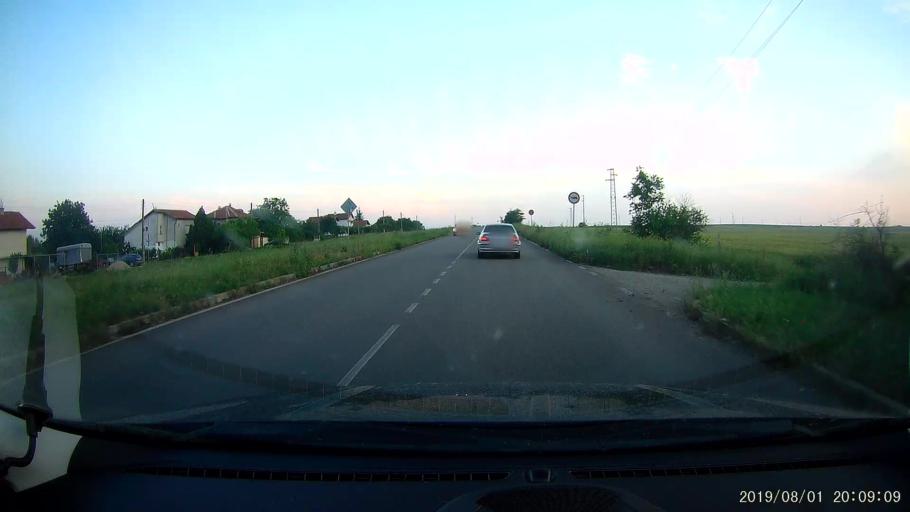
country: BG
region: Yambol
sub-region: Obshtina Yambol
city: Yambol
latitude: 42.5004
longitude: 26.5915
